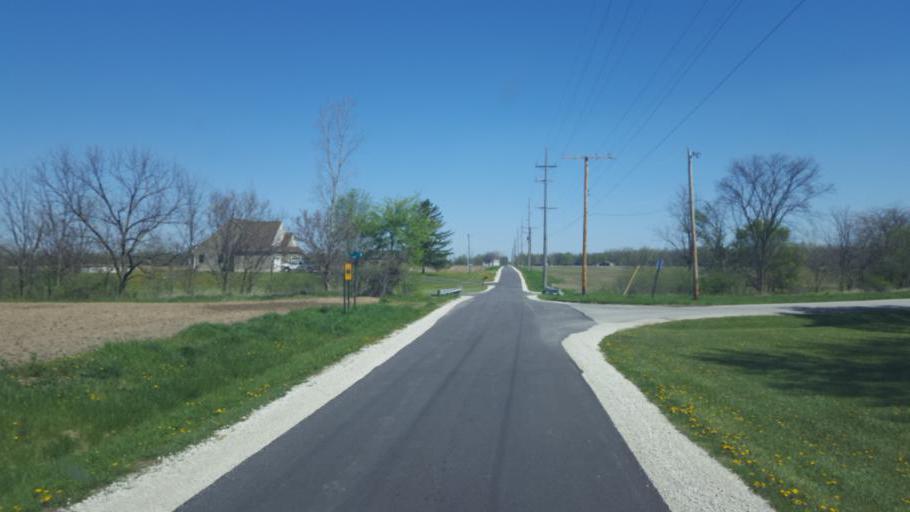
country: US
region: Ohio
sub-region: Sandusky County
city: Ballville
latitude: 41.2591
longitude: -83.1878
